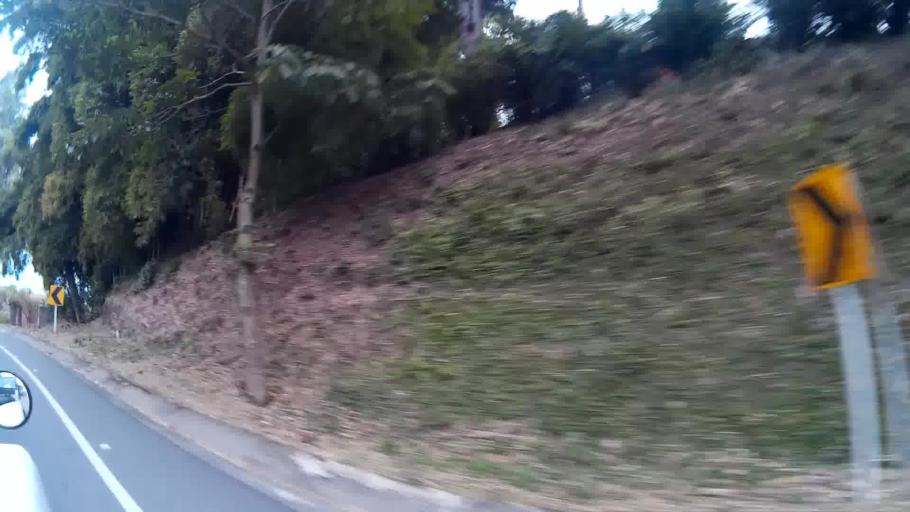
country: CO
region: Risaralda
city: Pereira
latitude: 4.7529
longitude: -75.6747
